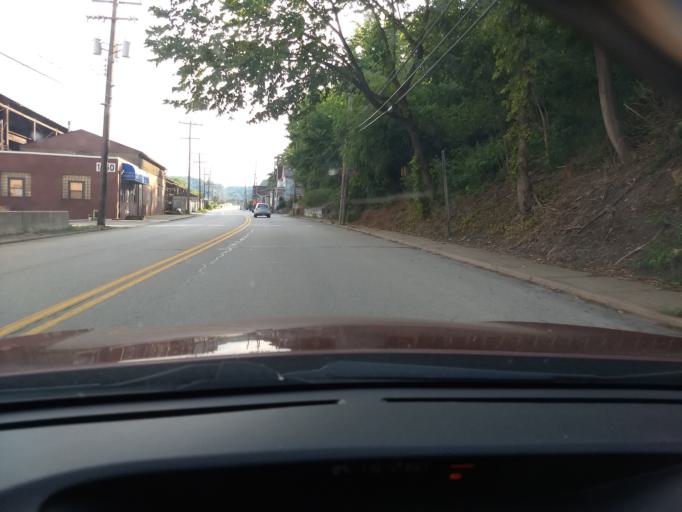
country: US
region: Pennsylvania
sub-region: Allegheny County
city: Tarentum
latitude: 40.5953
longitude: -79.7686
